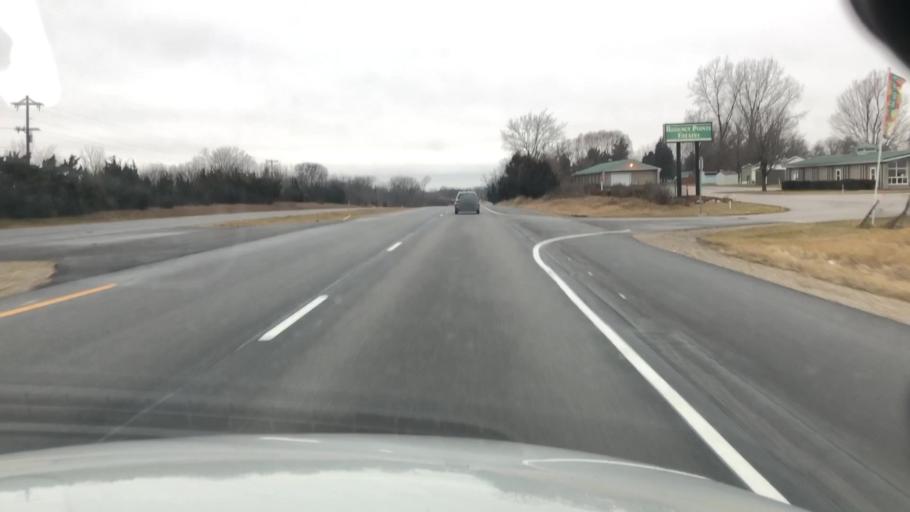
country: US
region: Indiana
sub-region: Kosciusko County
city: Pierceton
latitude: 41.1962
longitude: -85.6847
